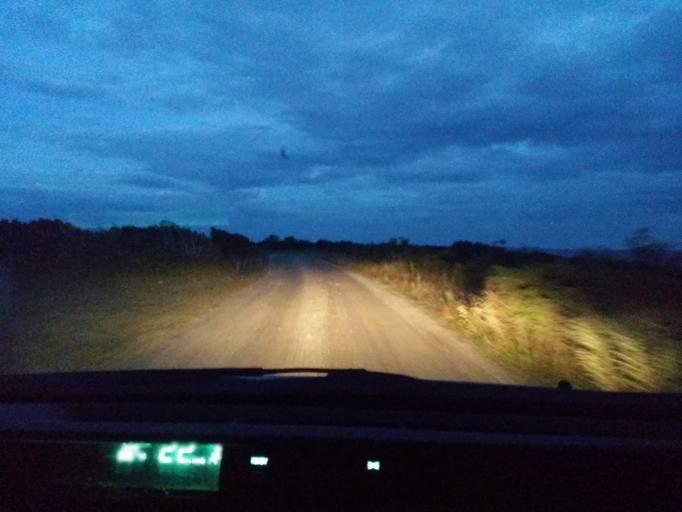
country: SE
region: Kalmar
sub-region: Borgholms Kommun
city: Borgholm
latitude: 57.1403
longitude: 16.9064
